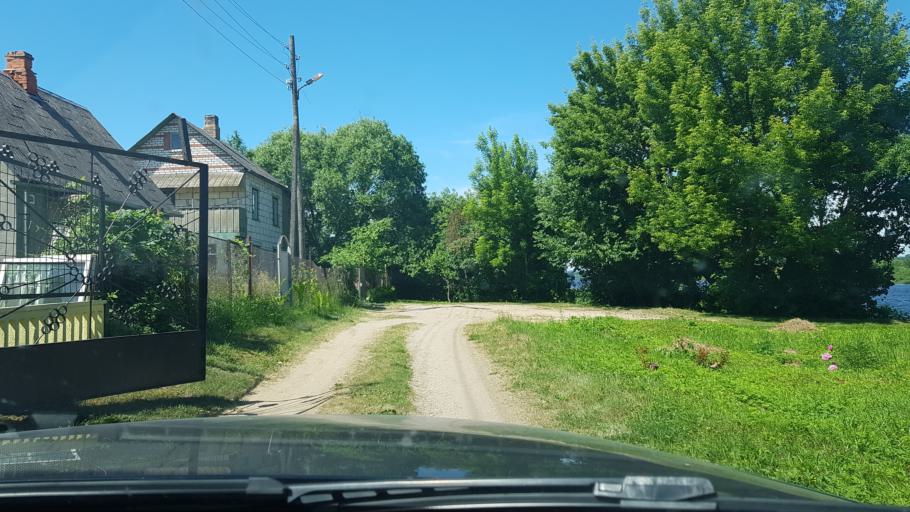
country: LV
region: Daugavpils
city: Daugavpils
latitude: 55.8601
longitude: 26.5676
